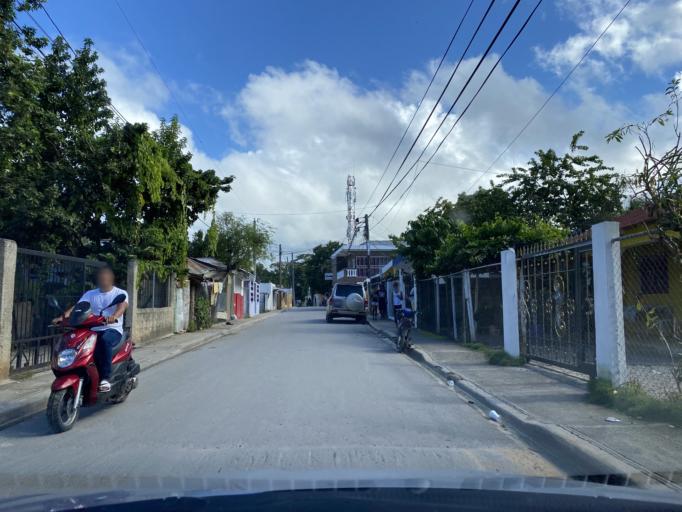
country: DO
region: Samana
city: Las Terrenas
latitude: 19.3079
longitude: -69.5445
